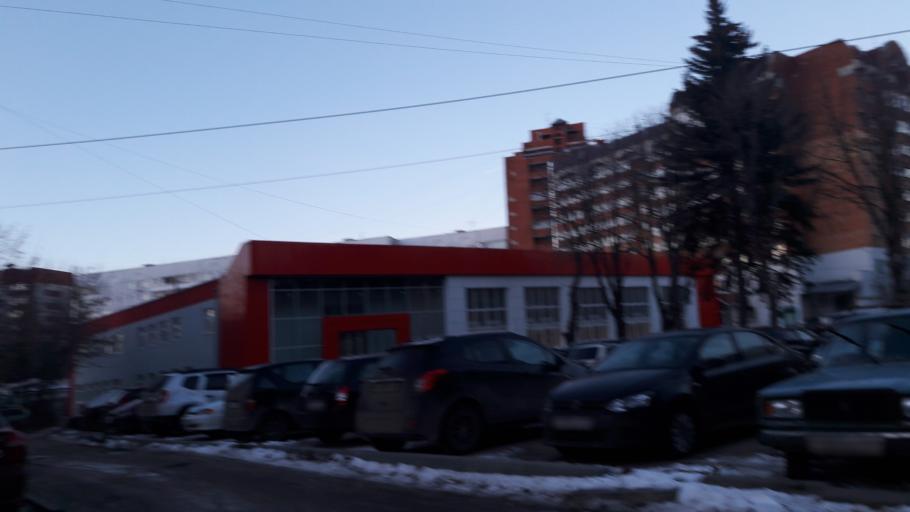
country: RU
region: Tula
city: Tula
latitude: 54.1913
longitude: 37.6115
